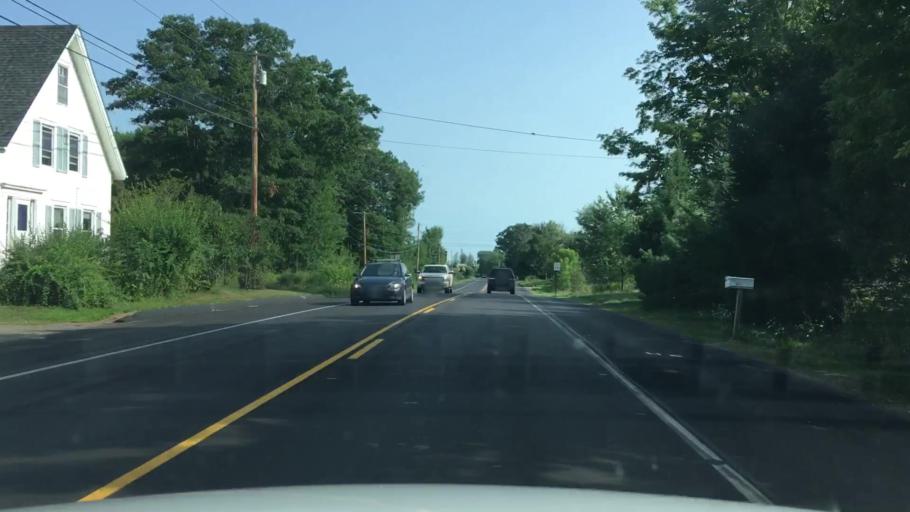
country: US
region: Maine
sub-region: Knox County
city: Warren
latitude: 44.1101
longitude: -69.2538
